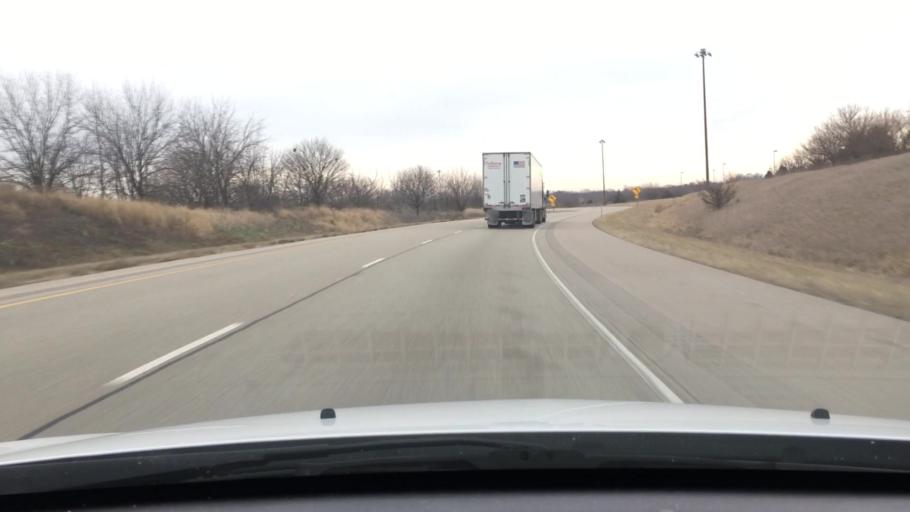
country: US
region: Illinois
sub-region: McLean County
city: Normal
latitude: 40.5380
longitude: -89.0132
